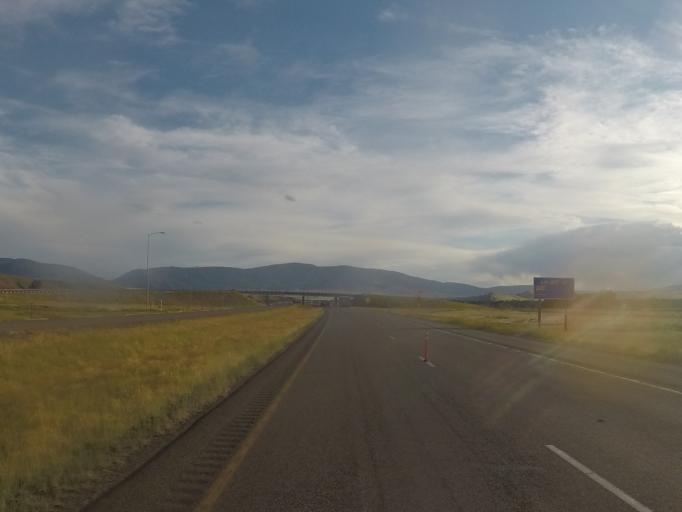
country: US
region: Montana
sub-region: Park County
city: Livingston
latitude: 45.6899
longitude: -110.4970
